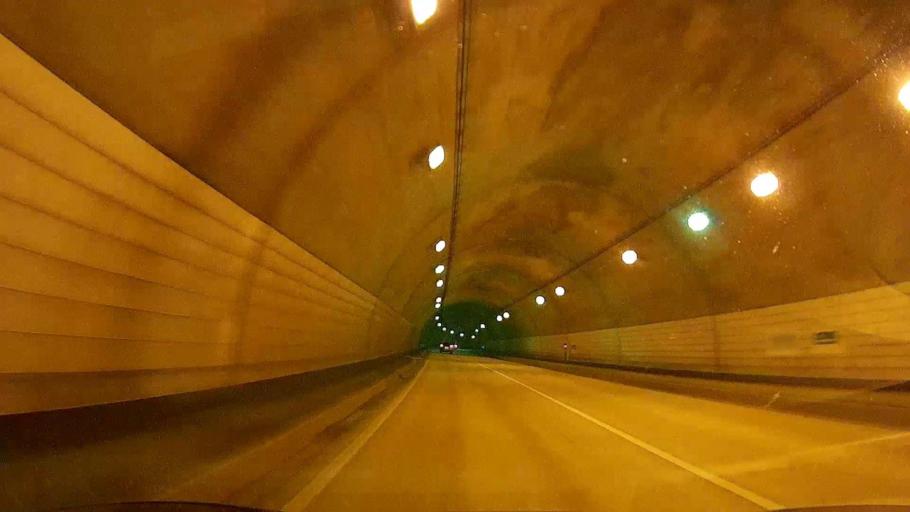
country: JP
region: Niigata
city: Tokamachi
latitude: 37.0074
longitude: 138.6426
